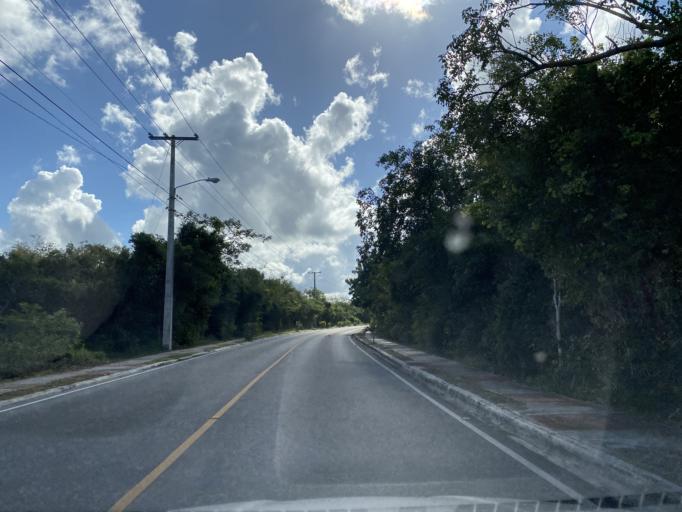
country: DO
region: La Altagracia
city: San Rafael del Yuma
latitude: 18.3421
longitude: -68.8136
